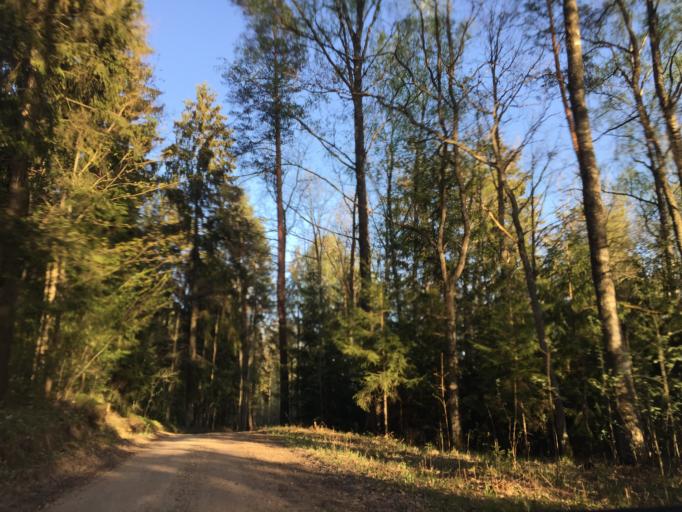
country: LV
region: Koknese
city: Koknese
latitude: 56.7173
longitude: 25.4853
